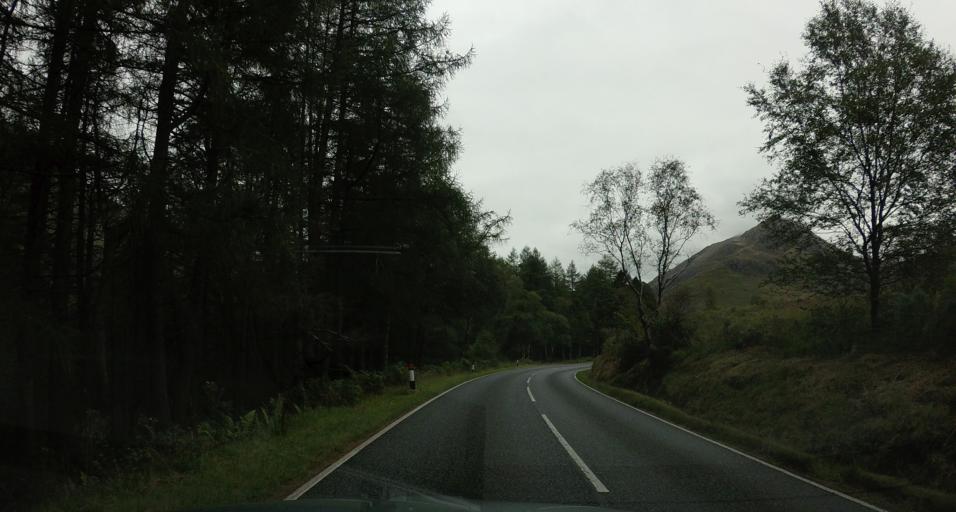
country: GB
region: Scotland
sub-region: Highland
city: Fort William
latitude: 56.7012
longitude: -5.0504
